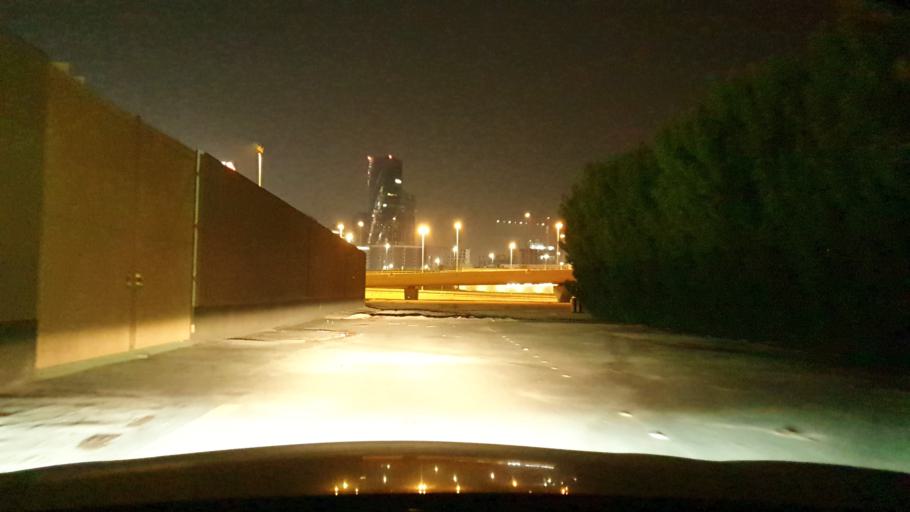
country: BH
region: Muharraq
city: Al Muharraq
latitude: 26.2534
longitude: 50.5841
